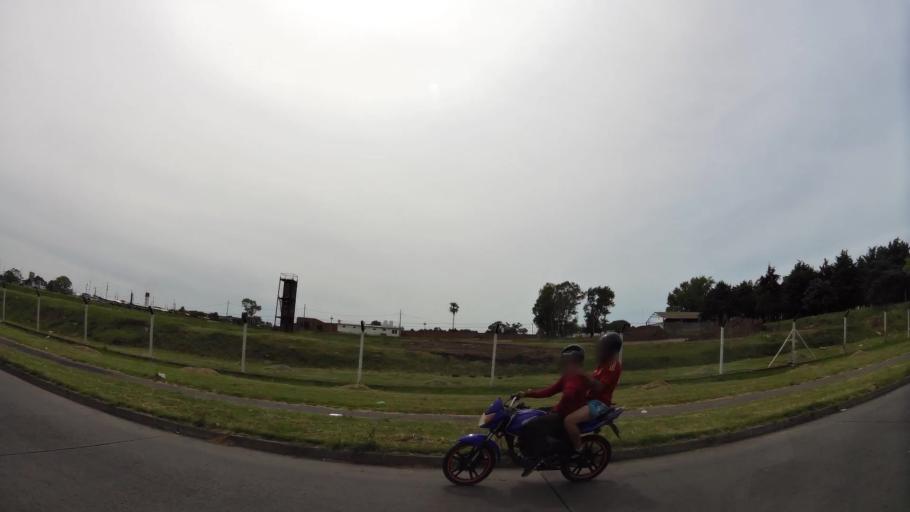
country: UY
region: Montevideo
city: Montevideo
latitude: -34.8456
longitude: -56.1697
